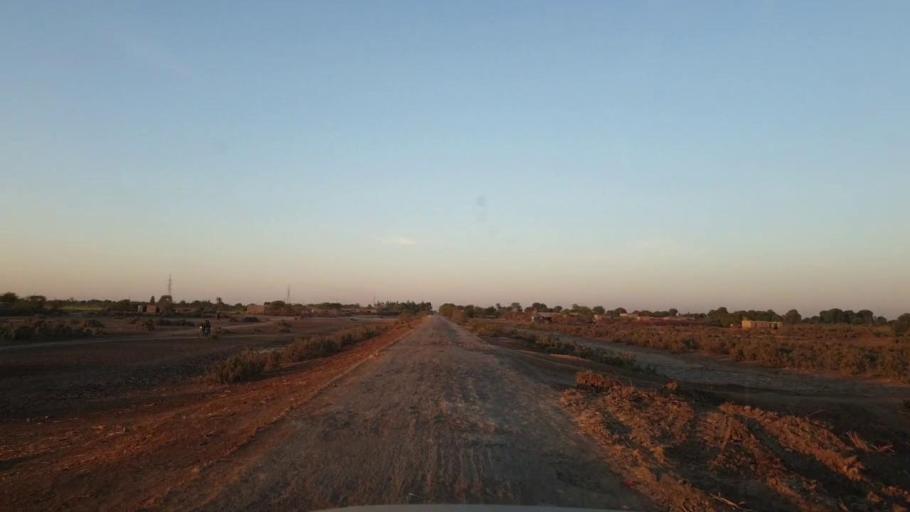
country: PK
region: Sindh
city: Kunri
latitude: 25.1417
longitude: 69.4447
